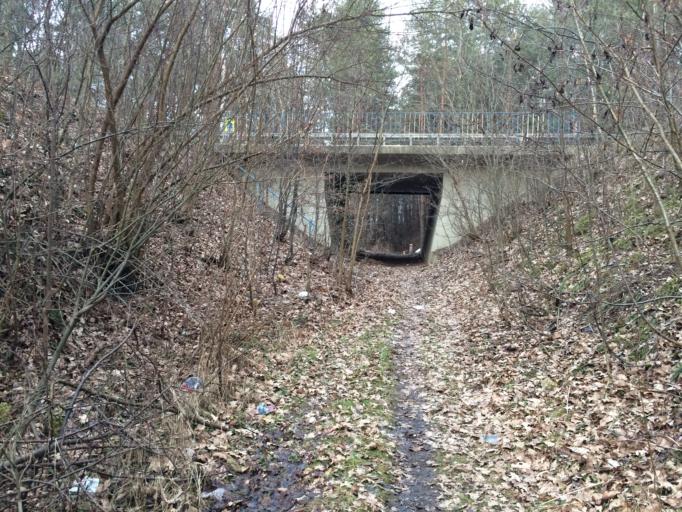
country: PL
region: Swietokrzyskie
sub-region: Powiat starachowicki
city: Starachowice
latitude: 51.0134
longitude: 21.0797
